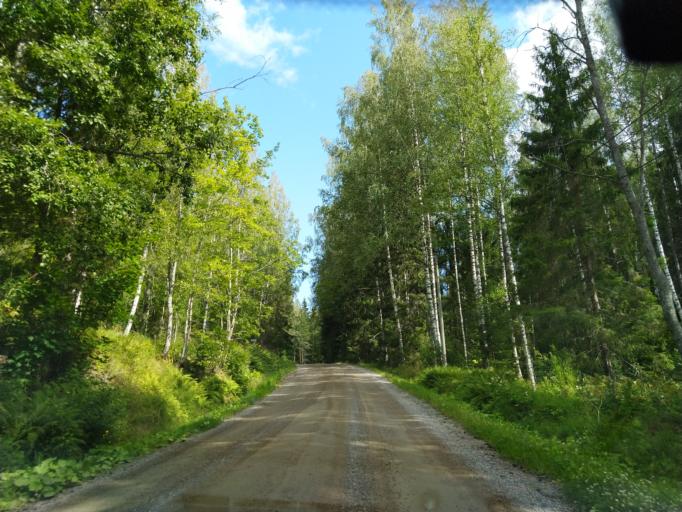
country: FI
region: Pirkanmaa
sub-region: Ylae-Pirkanmaa
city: Ruovesi
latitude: 61.9577
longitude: 24.0228
